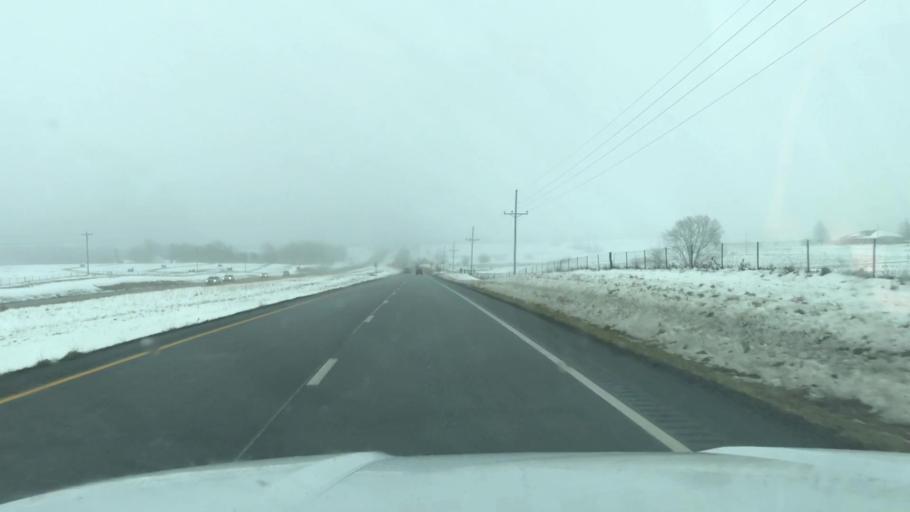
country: US
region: Missouri
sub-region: Clinton County
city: Cameron
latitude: 39.7539
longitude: -94.2743
